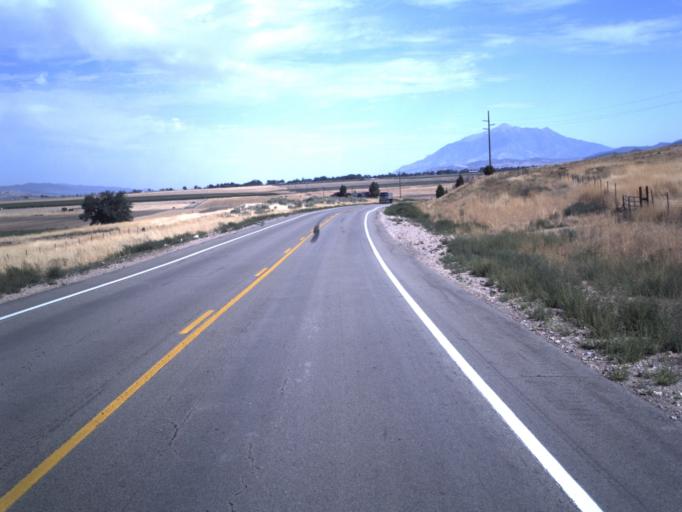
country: US
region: Utah
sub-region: Juab County
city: Nephi
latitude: 39.5214
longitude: -111.8678
